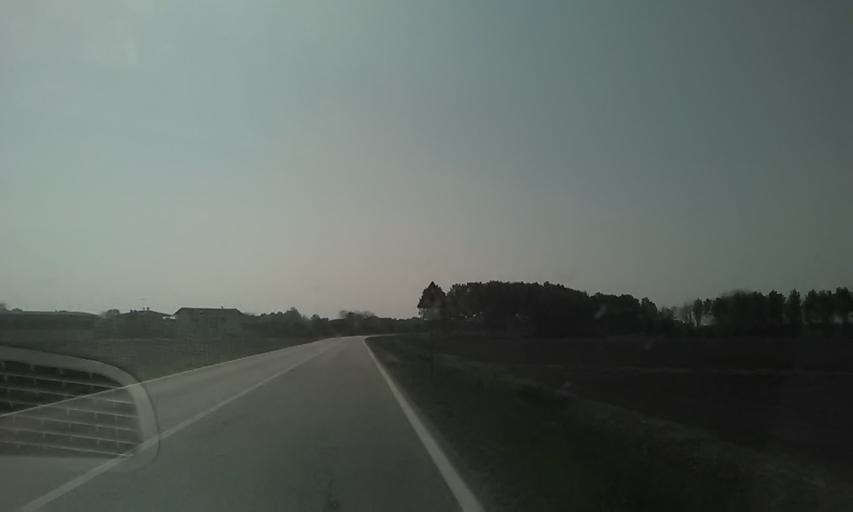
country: IT
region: Piedmont
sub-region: Provincia di Vercelli
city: Lenta
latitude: 45.5522
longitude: 8.3811
